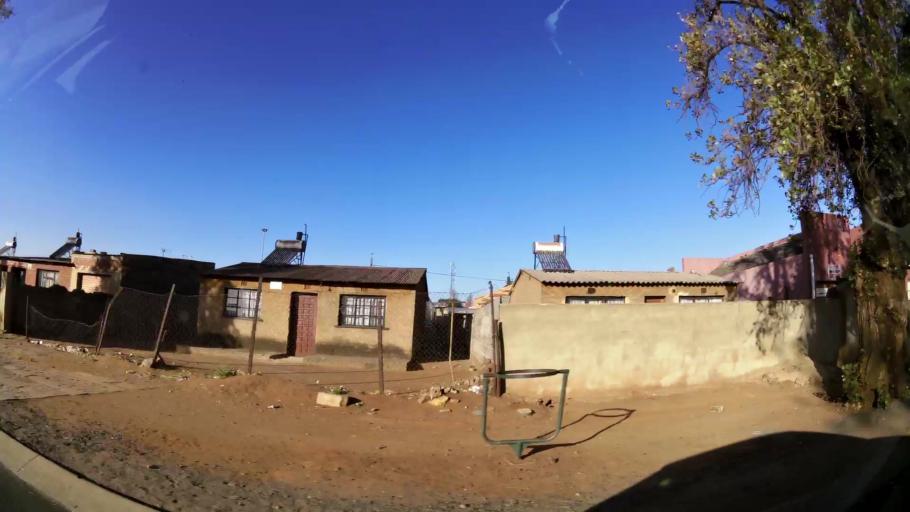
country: ZA
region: Gauteng
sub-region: Ekurhuleni Metropolitan Municipality
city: Tembisa
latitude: -26.0069
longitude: 28.2419
